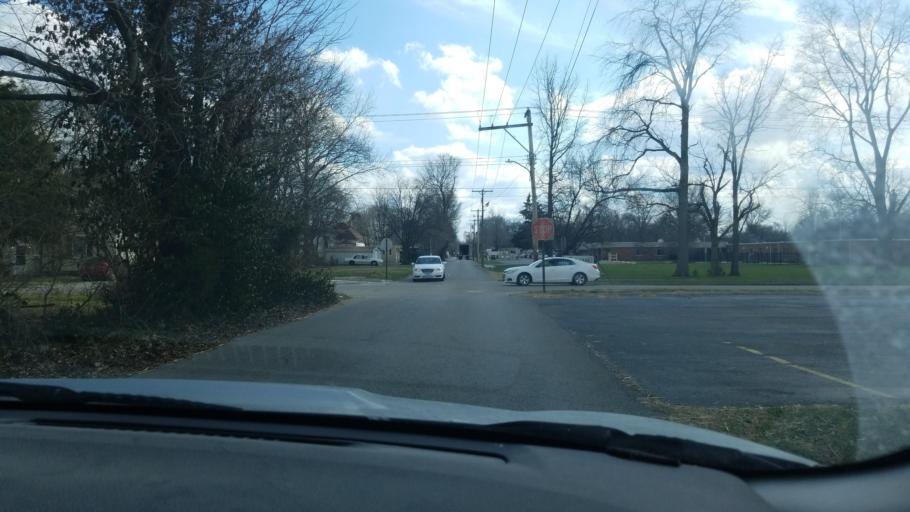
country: US
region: Illinois
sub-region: Saline County
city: Harrisburg
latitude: 37.7374
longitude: -88.5497
